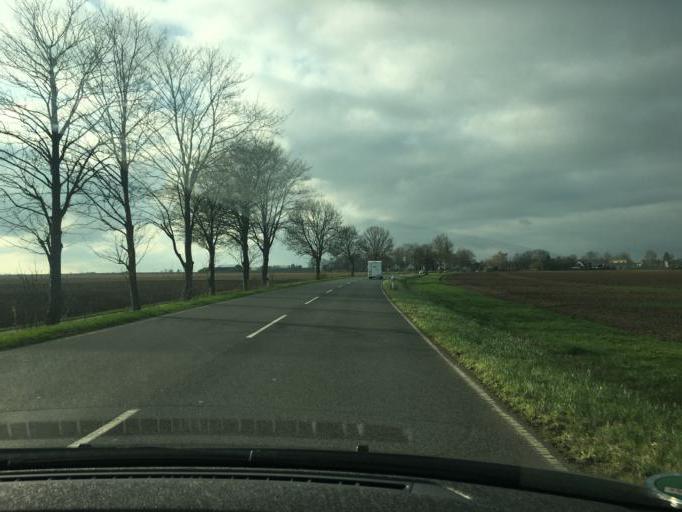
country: DE
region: North Rhine-Westphalia
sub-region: Regierungsbezirk Koln
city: Vettweiss
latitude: 50.7607
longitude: 6.6020
